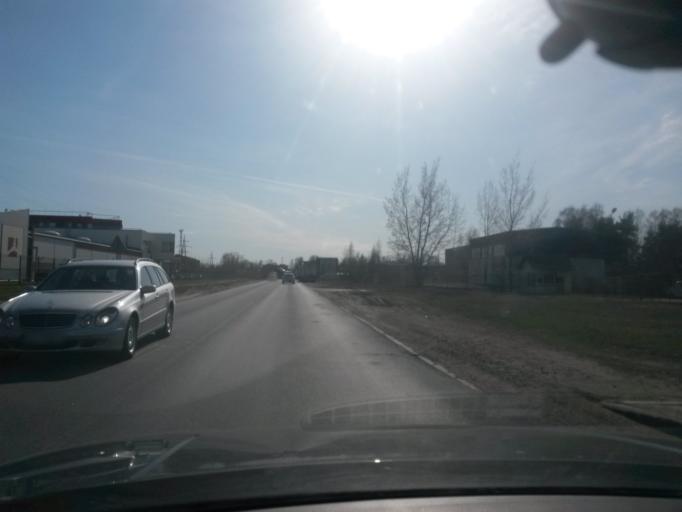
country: LV
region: Stopini
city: Ulbroka
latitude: 56.9117
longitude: 24.2169
